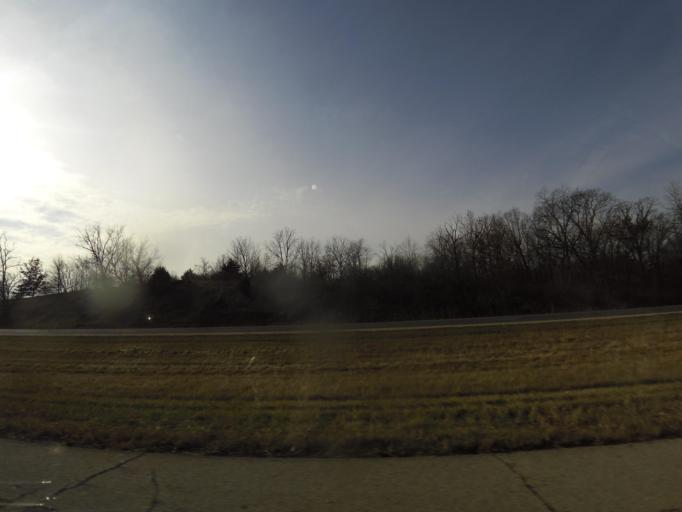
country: US
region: Illinois
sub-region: Macon County
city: Harristown
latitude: 39.8119
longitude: -89.0262
